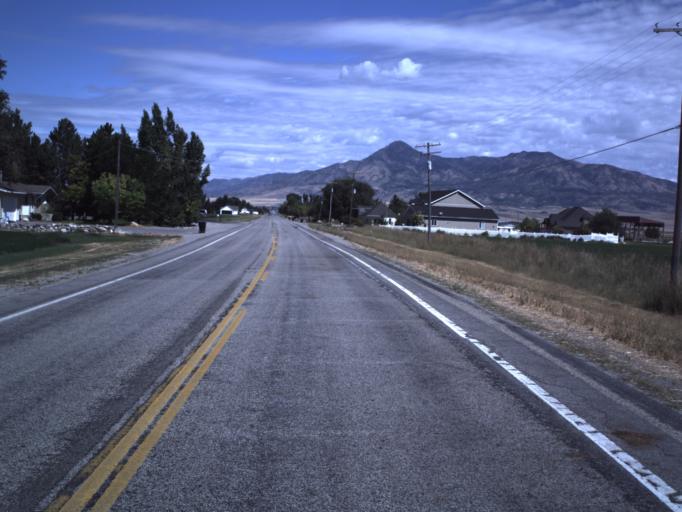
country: US
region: Utah
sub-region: Box Elder County
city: Garland
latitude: 41.8013
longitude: -112.1448
